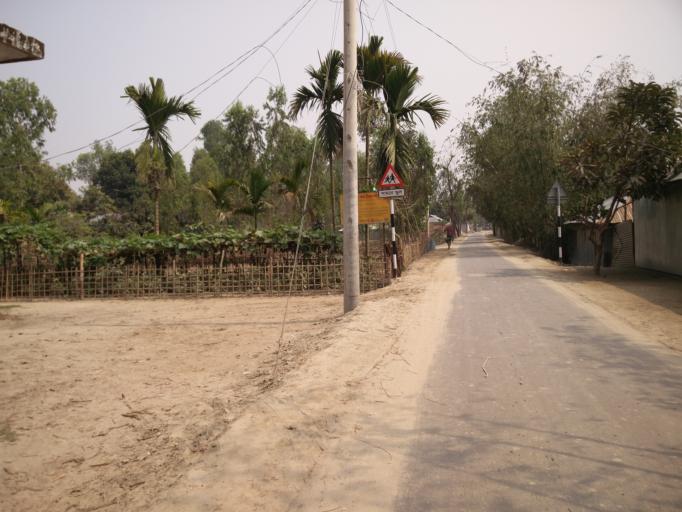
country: BD
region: Rangpur Division
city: Nageswari
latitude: 25.8866
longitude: 89.7367
